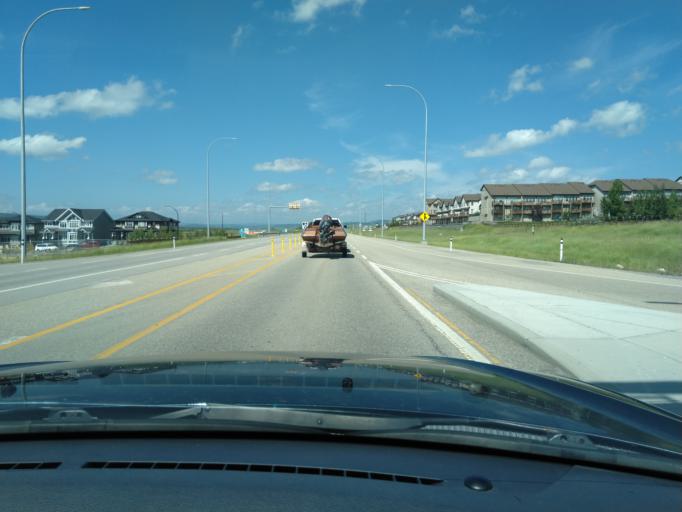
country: CA
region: Alberta
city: Cochrane
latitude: 51.2038
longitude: -114.5043
